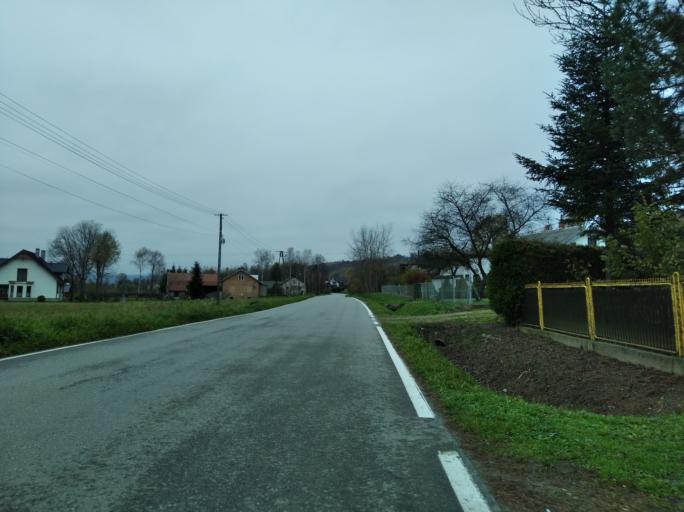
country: PL
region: Subcarpathian Voivodeship
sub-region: Powiat krosnienski
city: Leki
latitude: 49.8144
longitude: 21.6531
